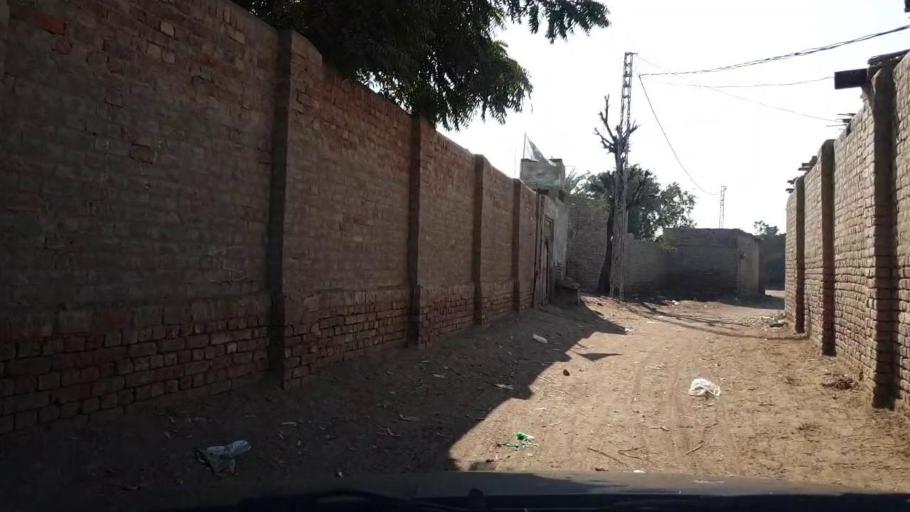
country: PK
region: Sindh
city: Jhol
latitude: 25.9323
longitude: 68.8286
